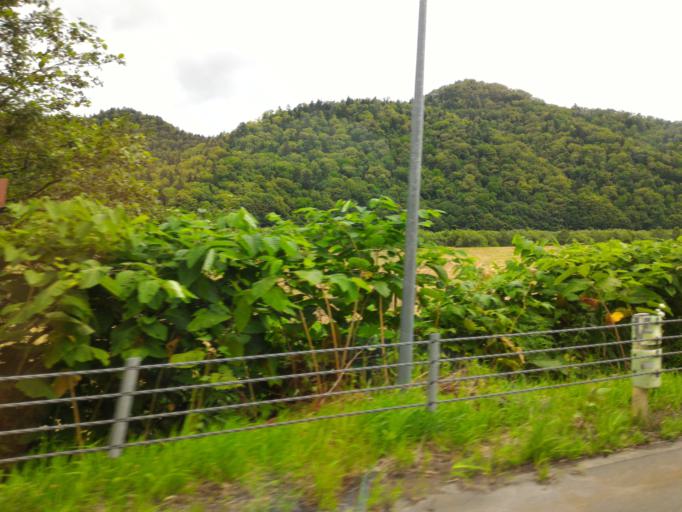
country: JP
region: Hokkaido
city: Nayoro
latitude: 44.7306
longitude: 142.2098
